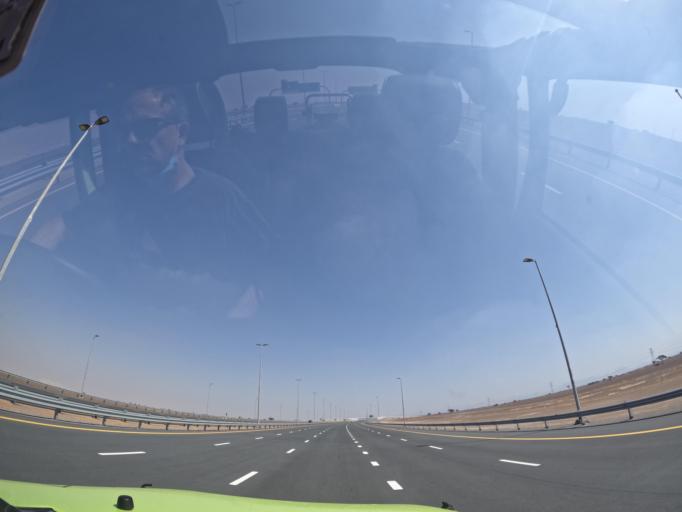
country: AE
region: Ash Shariqah
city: Adh Dhayd
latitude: 24.9240
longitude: 55.8078
